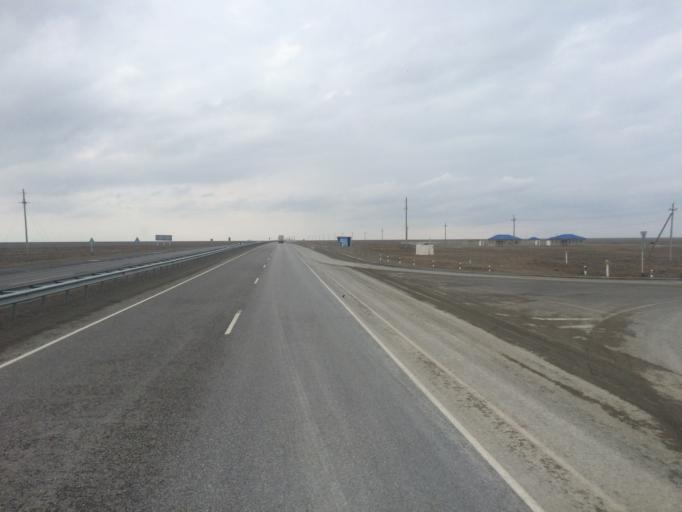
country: KZ
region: Qyzylorda
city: Shalqiya
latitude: 43.6061
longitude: 67.6713
